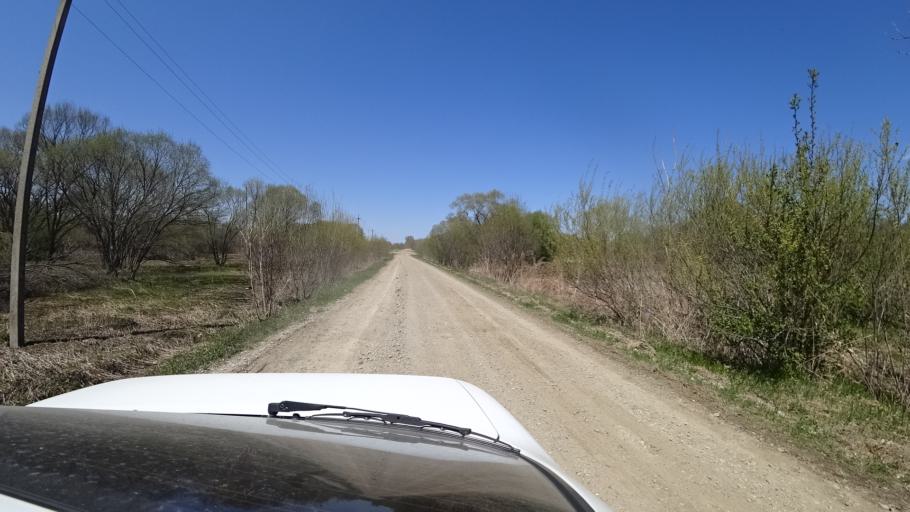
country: RU
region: Primorskiy
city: Lazo
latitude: 45.7946
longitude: 133.7631
